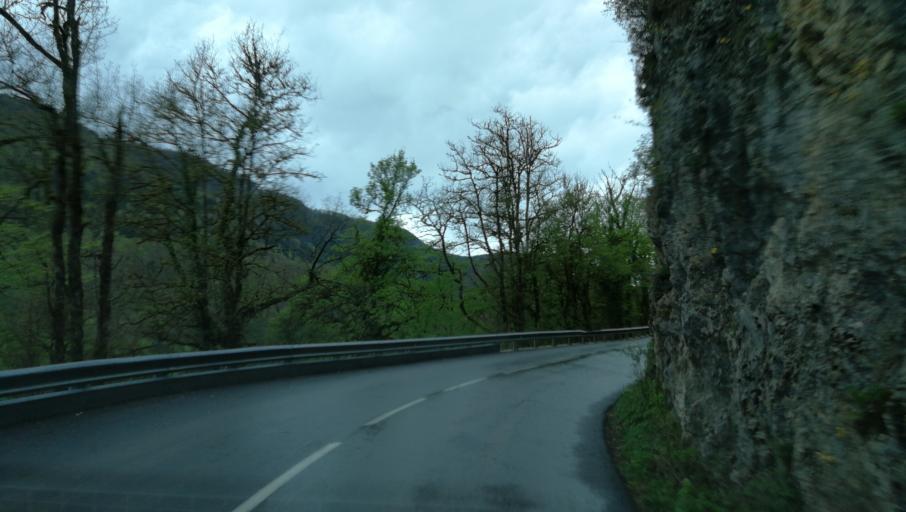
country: FR
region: Franche-Comte
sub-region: Departement du Jura
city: Saint-Claude
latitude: 46.3620
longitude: 5.8542
